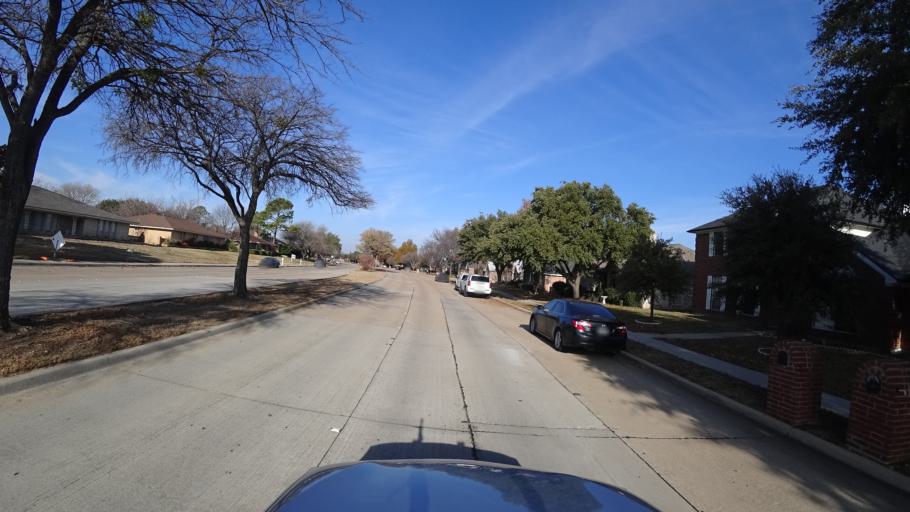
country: US
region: Texas
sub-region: Denton County
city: Lewisville
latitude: 33.0501
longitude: -97.0217
